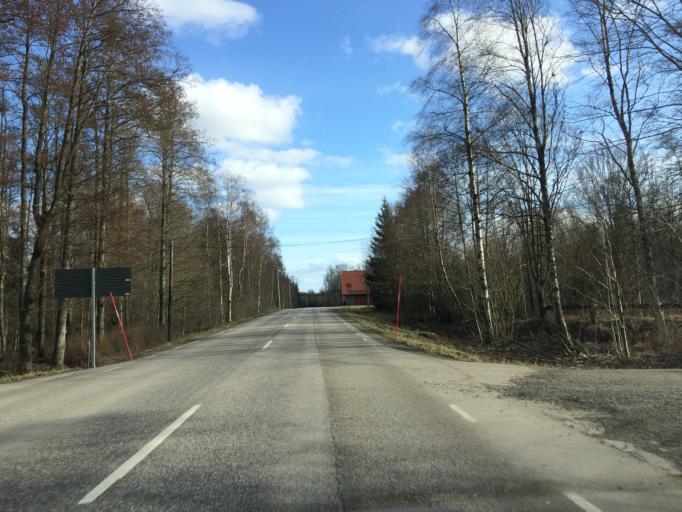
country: SE
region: Kronoberg
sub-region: Almhults Kommun
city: AElmhult
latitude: 56.5727
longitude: 14.1158
